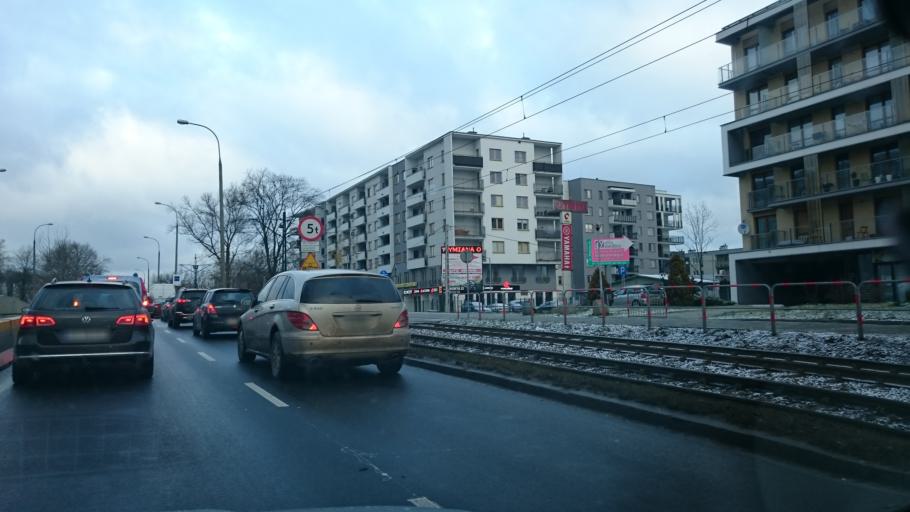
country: PL
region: Lesser Poland Voivodeship
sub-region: Krakow
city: Krakow
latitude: 50.0365
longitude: 19.9670
